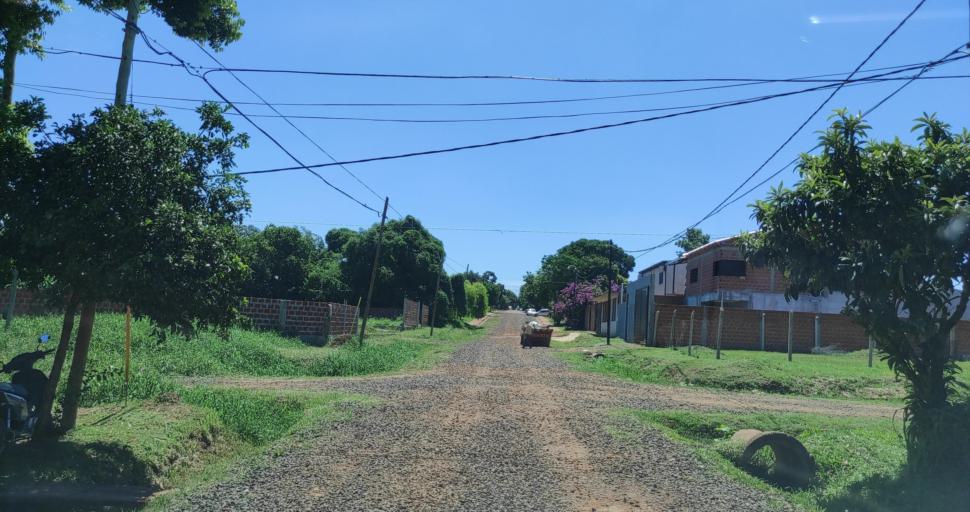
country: AR
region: Misiones
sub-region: Departamento de Capital
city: Posadas
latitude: -27.4083
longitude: -55.9169
